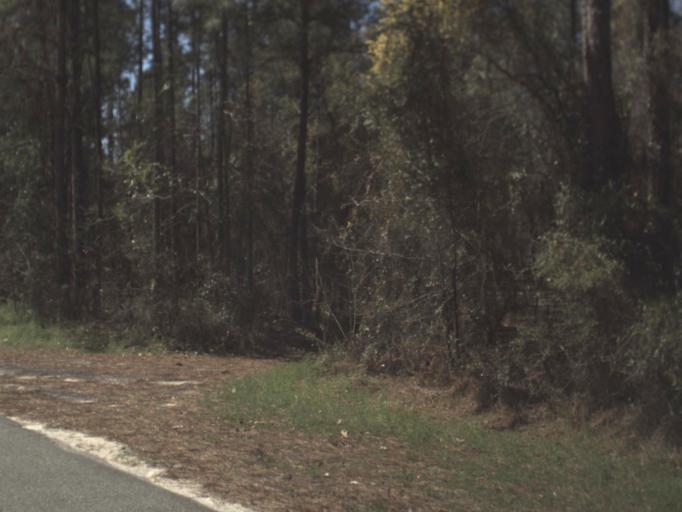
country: US
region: Florida
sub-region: Leon County
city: Woodville
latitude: 30.3070
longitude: -84.3119
